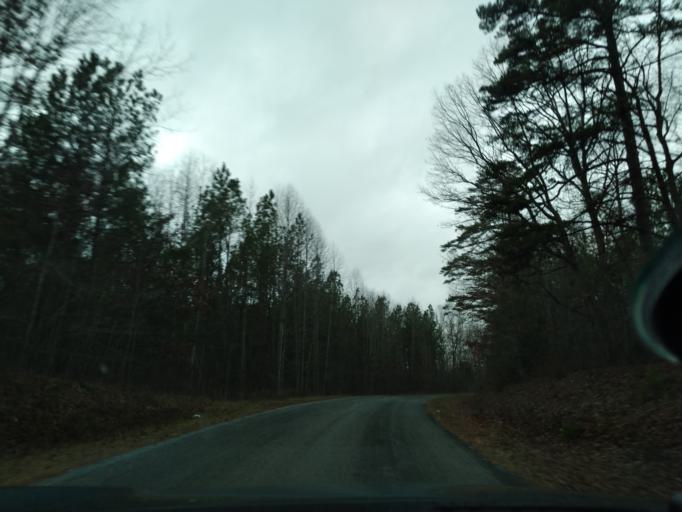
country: US
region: Virginia
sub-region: Buckingham County
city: Buckingham
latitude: 37.4212
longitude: -78.6621
